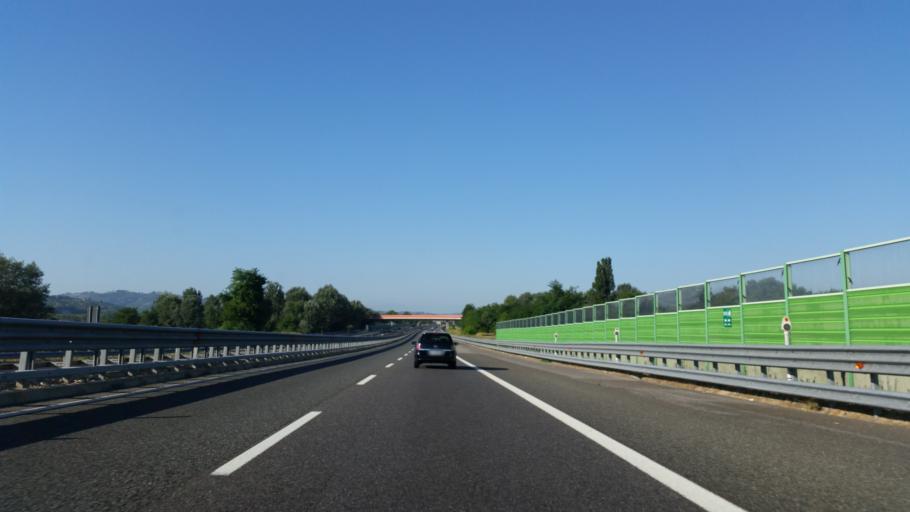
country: IT
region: Piedmont
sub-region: Provincia di Cuneo
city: Vaccheria
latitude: 44.7289
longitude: 8.0569
